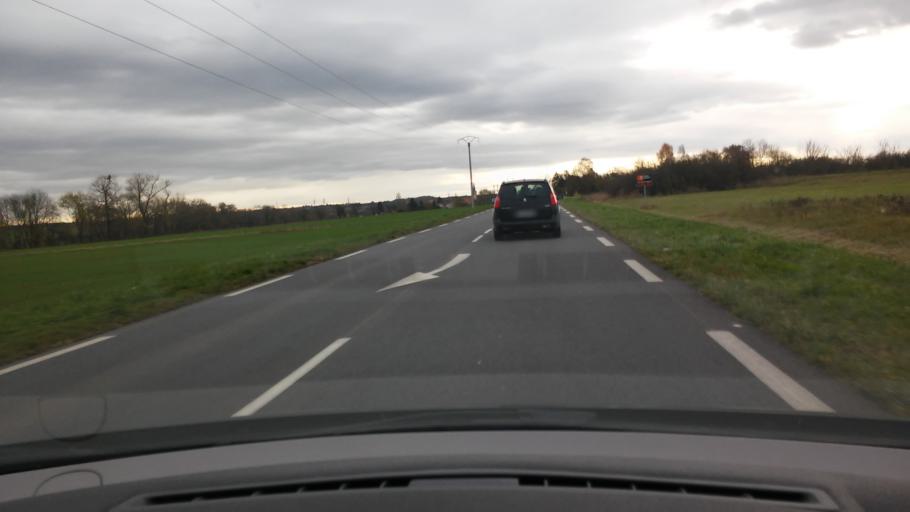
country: FR
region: Lorraine
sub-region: Departement de la Moselle
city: Argancy
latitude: 49.1832
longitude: 6.2077
